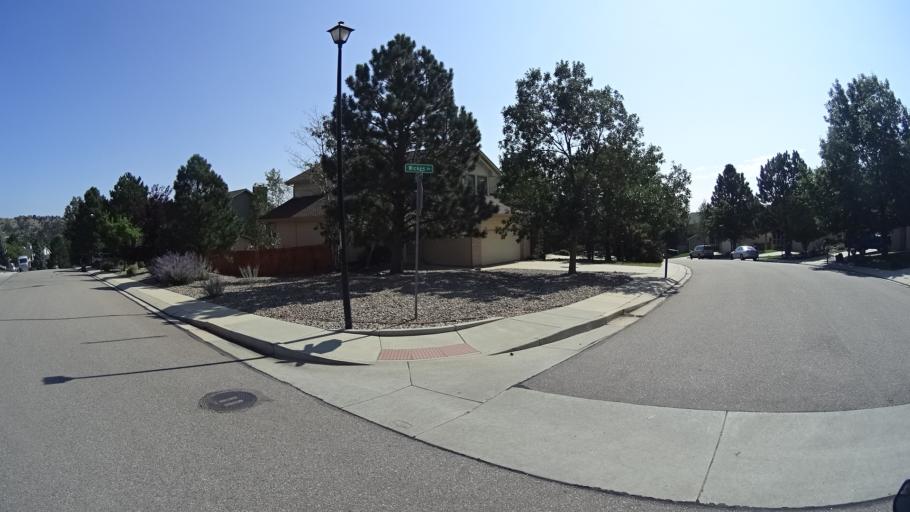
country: US
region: Colorado
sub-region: El Paso County
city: Air Force Academy
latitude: 38.9205
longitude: -104.8679
